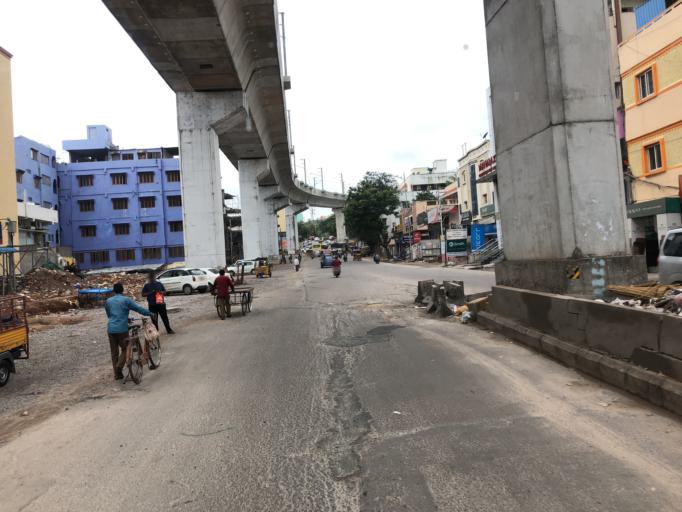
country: IN
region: Telangana
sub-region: Rangareddi
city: Kukatpalli
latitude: 17.4315
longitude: 78.4259
